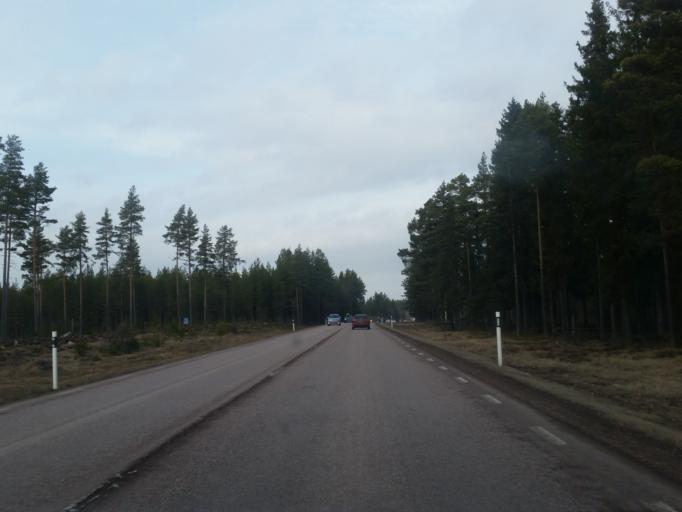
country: SE
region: Dalarna
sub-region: Mora Kommun
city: Mora
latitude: 60.9713
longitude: 14.6997
